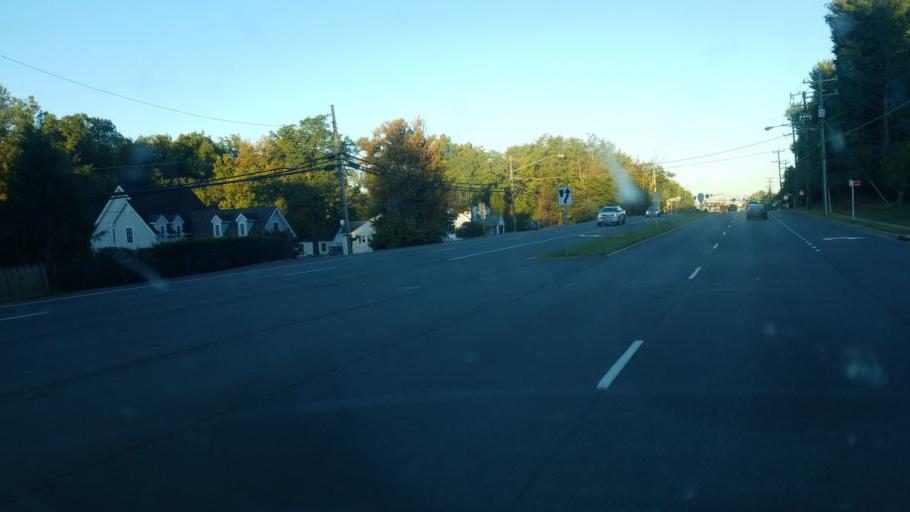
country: US
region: Virginia
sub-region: Fairfax County
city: Annandale
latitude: 38.8264
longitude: -77.1766
